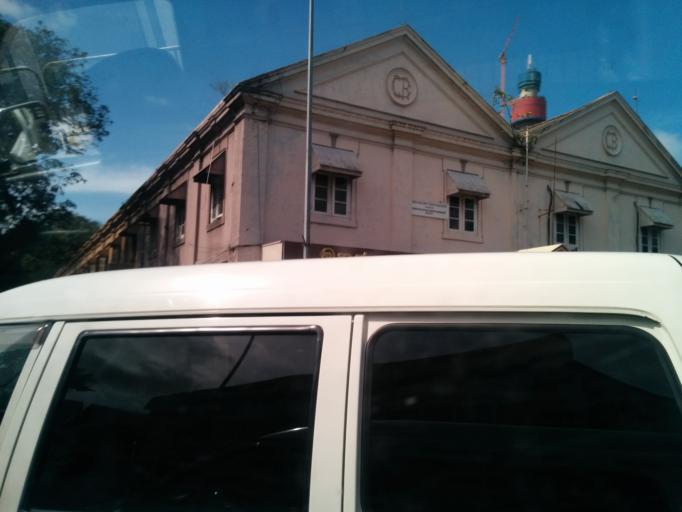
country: LK
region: Western
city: Colombo
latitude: 6.9322
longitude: 79.8577
